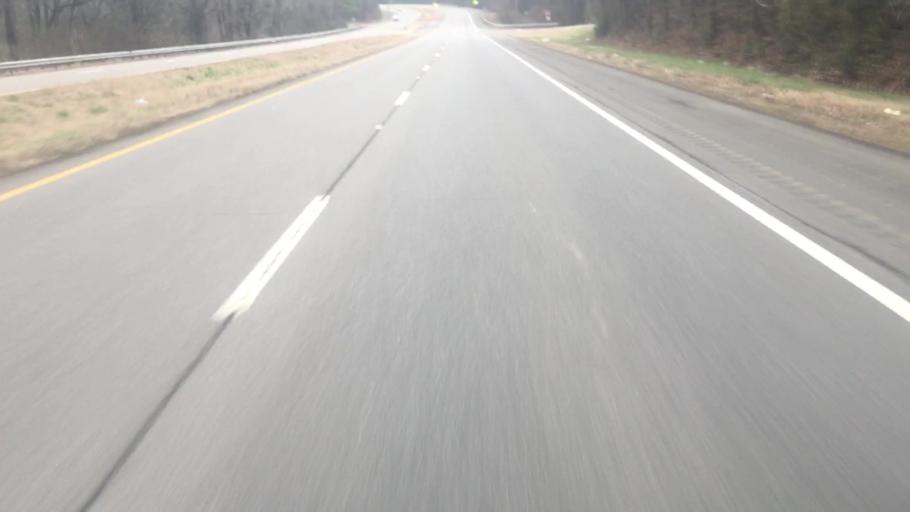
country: US
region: Alabama
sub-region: Walker County
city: Cordova
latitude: 33.8231
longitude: -87.1910
